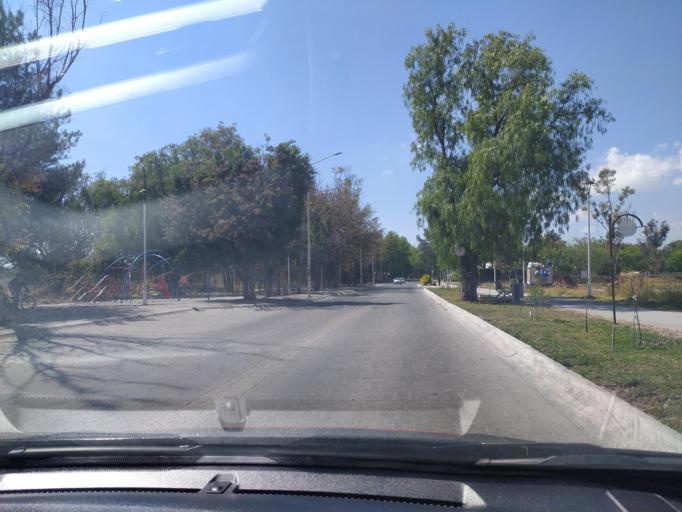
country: LA
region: Oudomxai
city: Muang La
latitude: 21.0265
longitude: 101.8347
